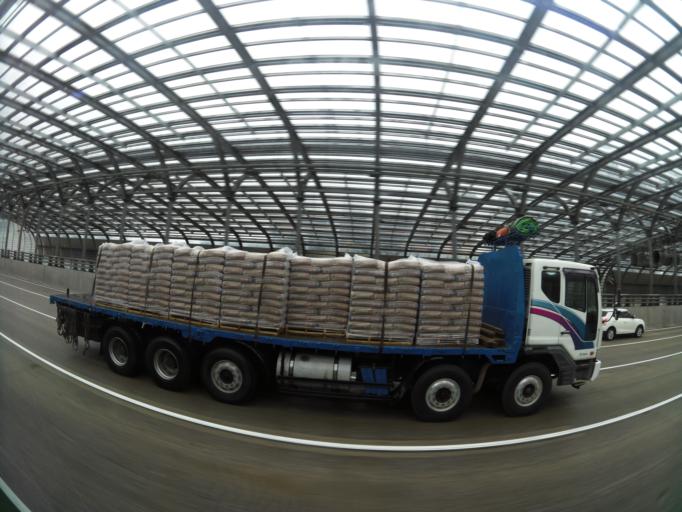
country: KR
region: Gyeonggi-do
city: Suwon-si
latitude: 37.2940
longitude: 127.0759
